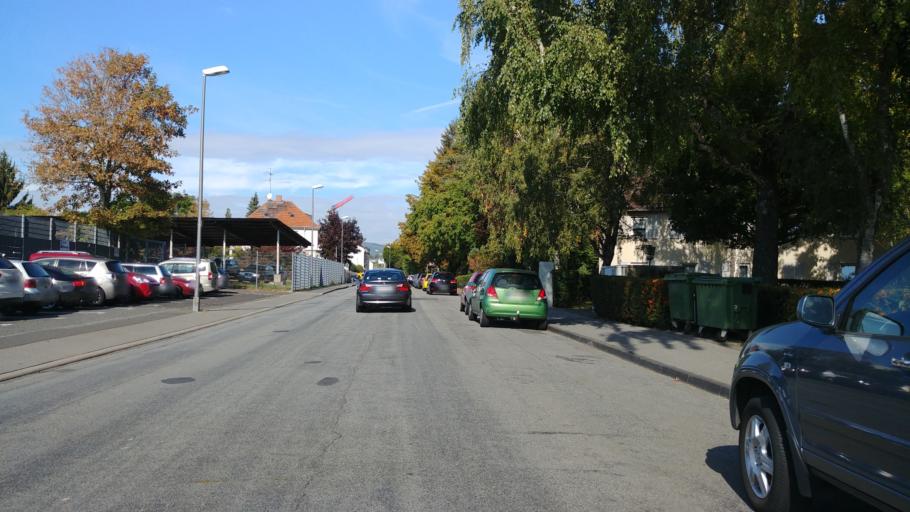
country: DE
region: Hesse
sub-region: Regierungsbezirk Darmstadt
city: Wiesbaden
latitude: 50.0738
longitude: 8.2105
